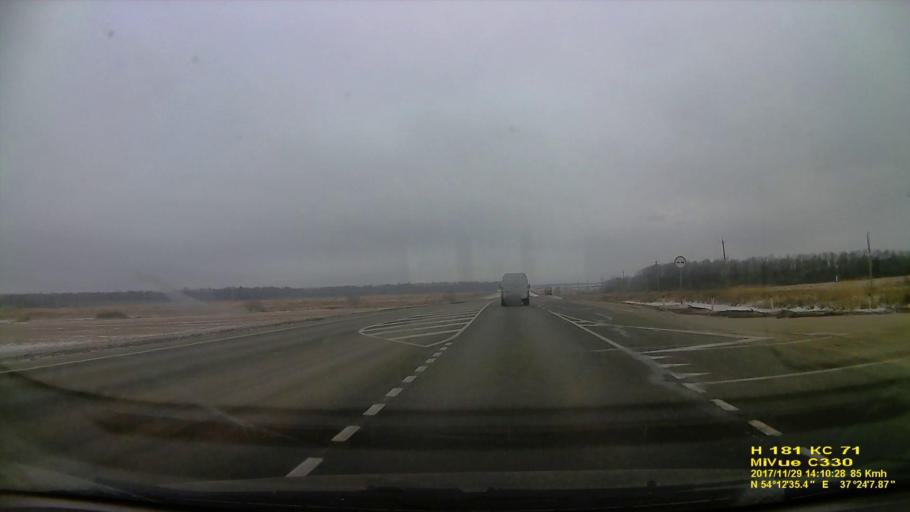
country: RU
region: Tula
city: Leninskiy
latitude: 54.2096
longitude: 37.4025
